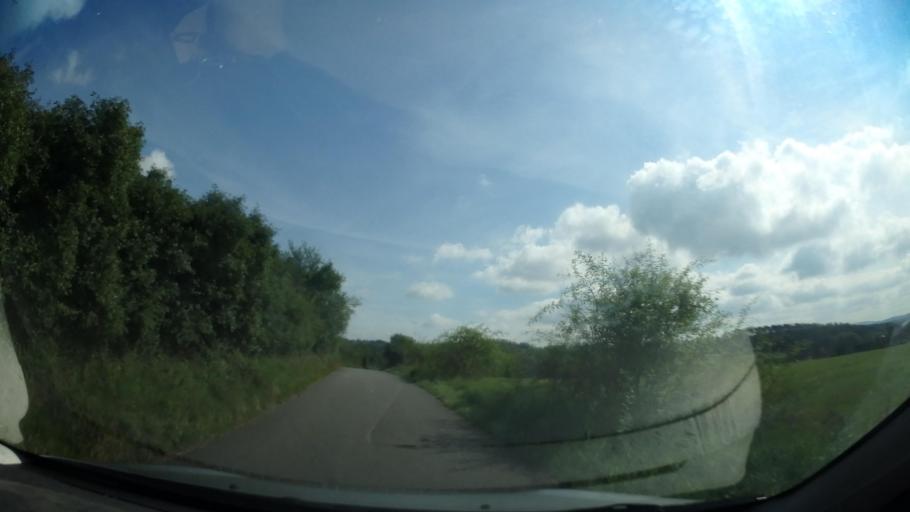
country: CZ
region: Central Bohemia
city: Krasna Hora nad Vltavou
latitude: 49.6790
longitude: 14.3174
